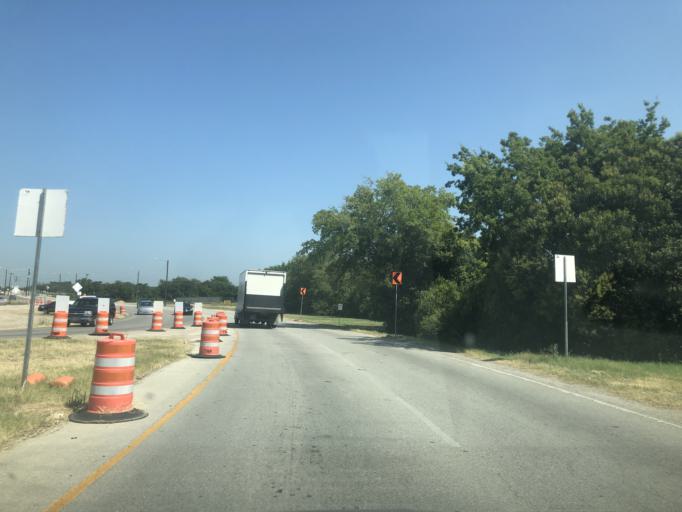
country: US
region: Texas
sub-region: Tarrant County
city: Fort Worth
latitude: 32.7605
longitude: -97.3444
